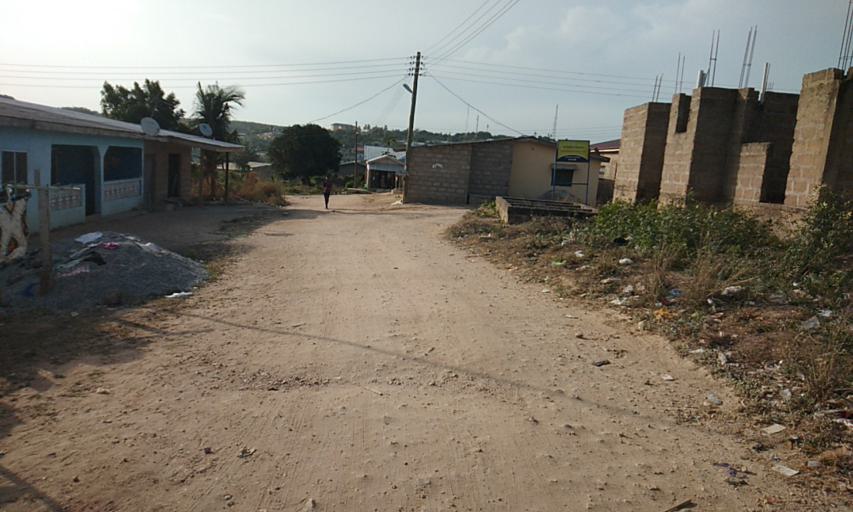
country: GH
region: Central
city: Winneba
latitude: 5.3587
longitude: -0.6150
